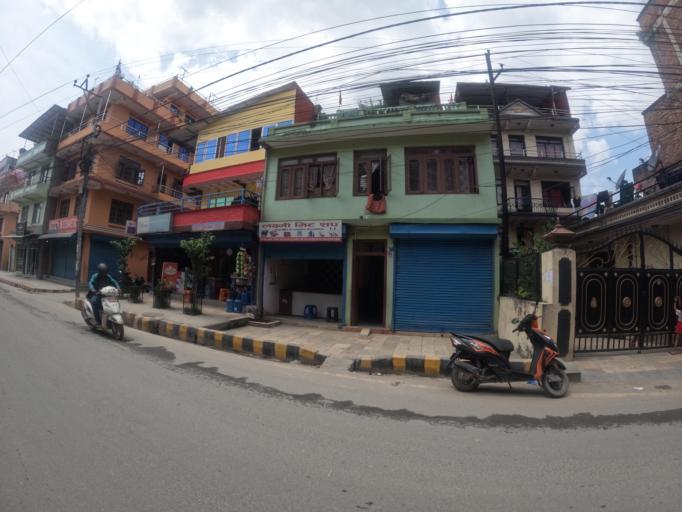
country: NP
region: Central Region
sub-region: Bagmati Zone
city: Bhaktapur
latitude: 27.6874
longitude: 85.3884
